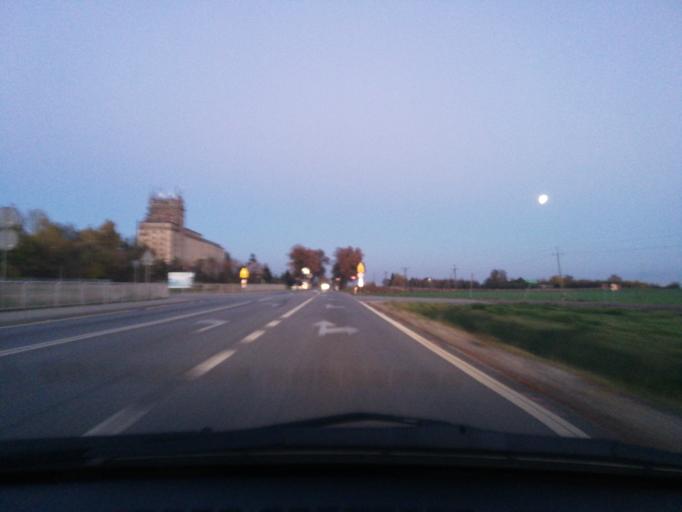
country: PL
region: Lodz Voivodeship
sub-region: Powiat brzezinski
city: Rogow
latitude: 51.8065
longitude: 19.8759
